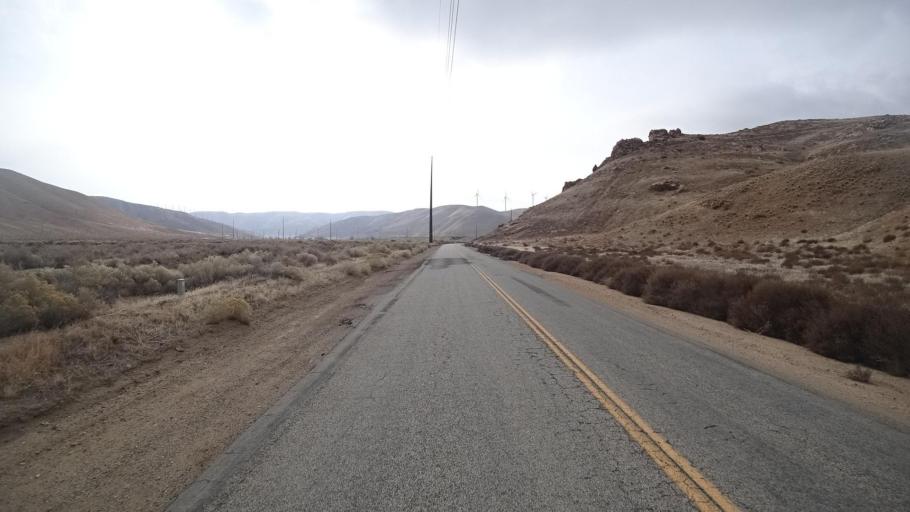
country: US
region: California
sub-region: Kern County
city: Tehachapi
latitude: 35.1157
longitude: -118.3238
